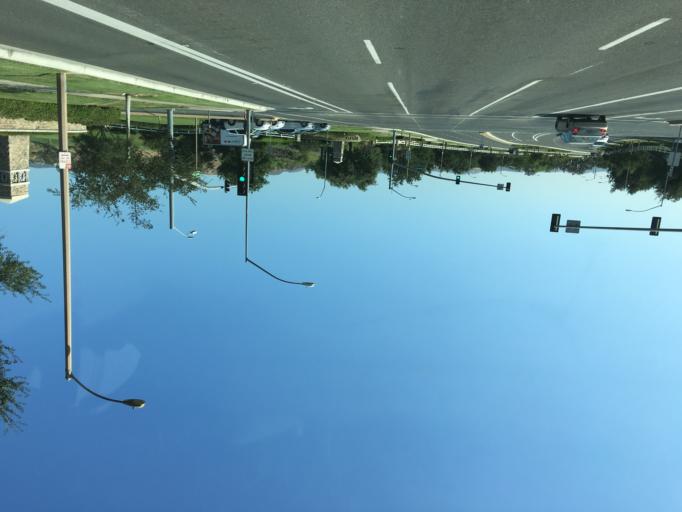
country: US
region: California
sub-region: Los Angeles County
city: Santa Clarita
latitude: 34.4080
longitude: -118.5799
